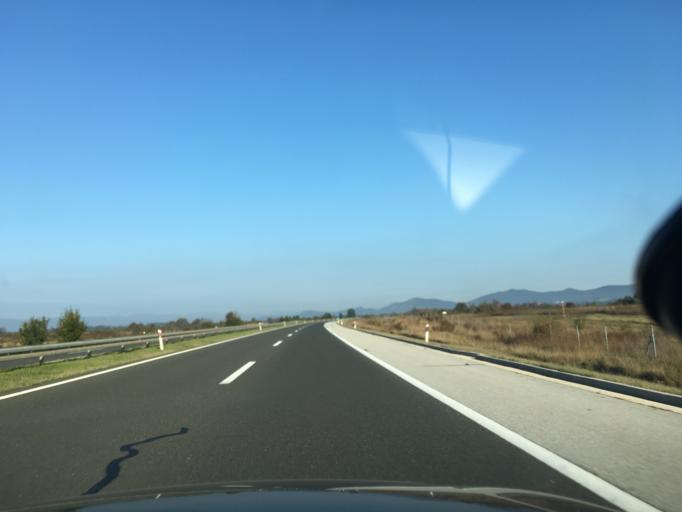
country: HR
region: Licko-Senjska
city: Gospic
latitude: 44.4869
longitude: 15.5470
